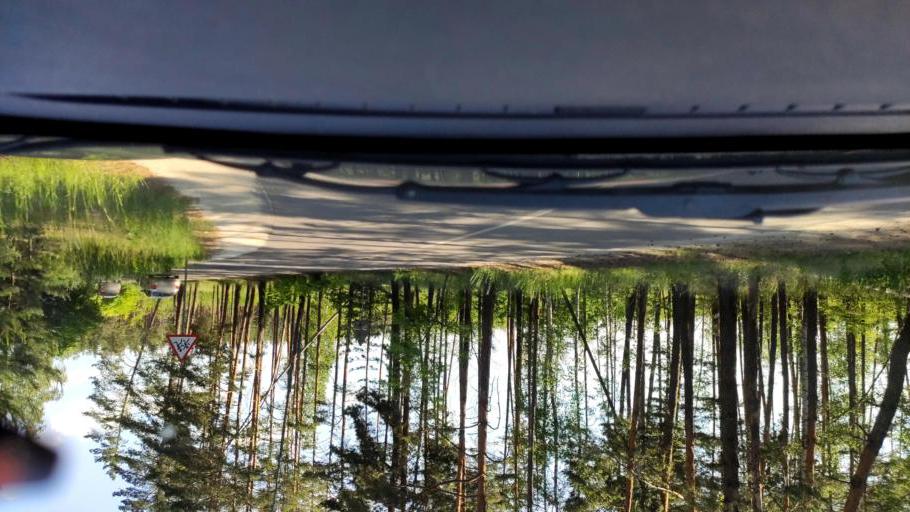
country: RU
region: Voronezj
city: Somovo
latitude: 51.7592
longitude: 39.3657
